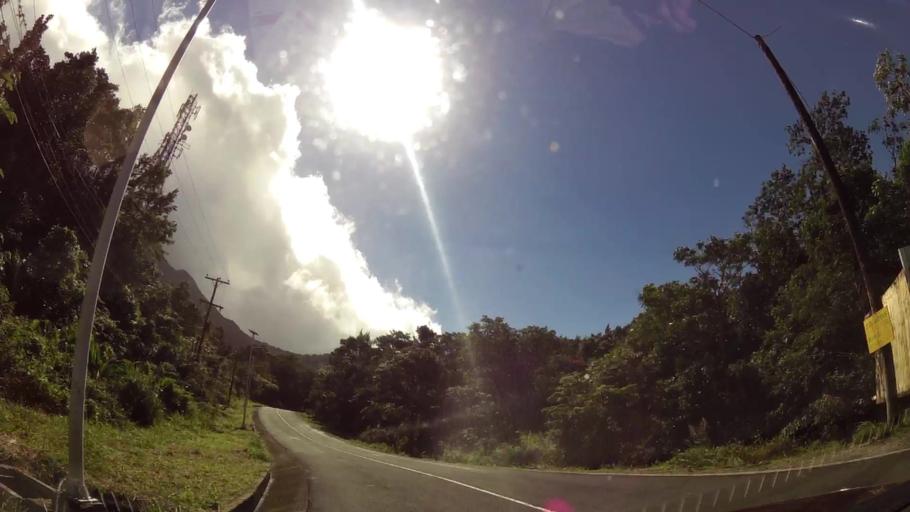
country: DM
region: Saint Paul
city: Pont Casse
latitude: 15.3773
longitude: -61.3444
